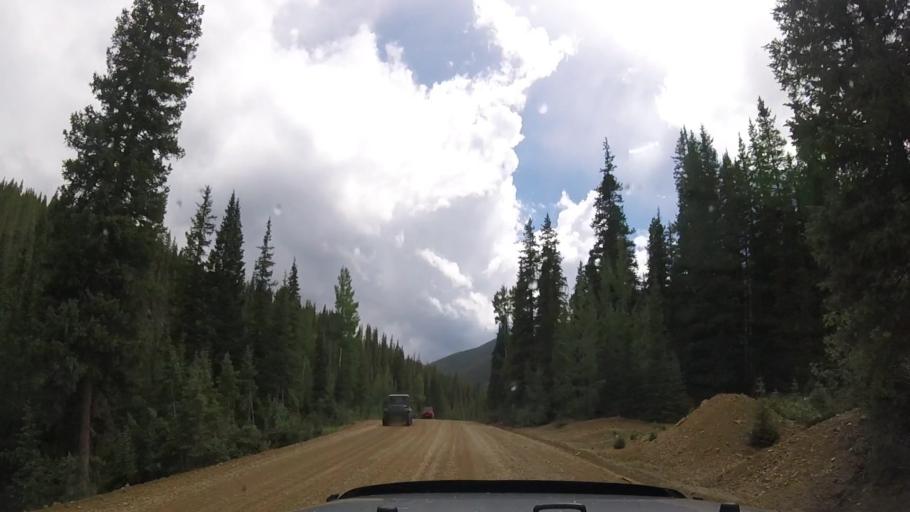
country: US
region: Colorado
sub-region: San Juan County
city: Silverton
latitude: 37.8455
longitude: -107.6789
